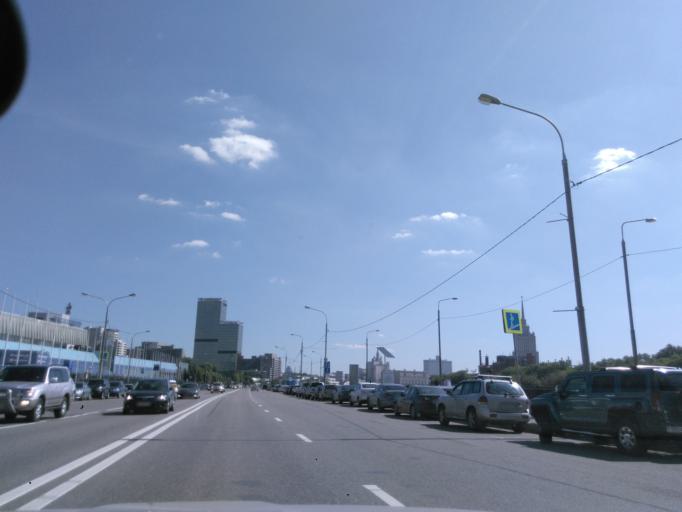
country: RU
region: Moskovskaya
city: Presnenskiy
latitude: 55.7487
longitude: 37.5459
